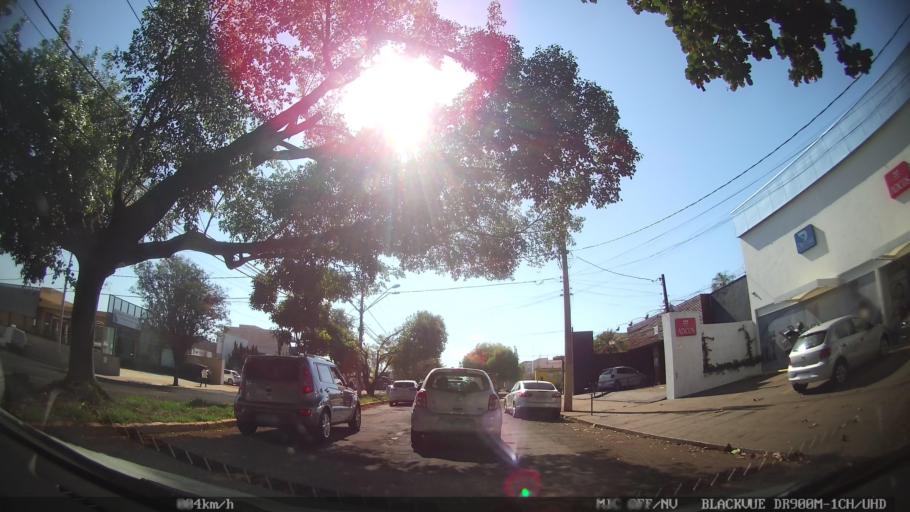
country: BR
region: Sao Paulo
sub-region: Ribeirao Preto
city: Ribeirao Preto
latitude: -21.1960
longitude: -47.8135
